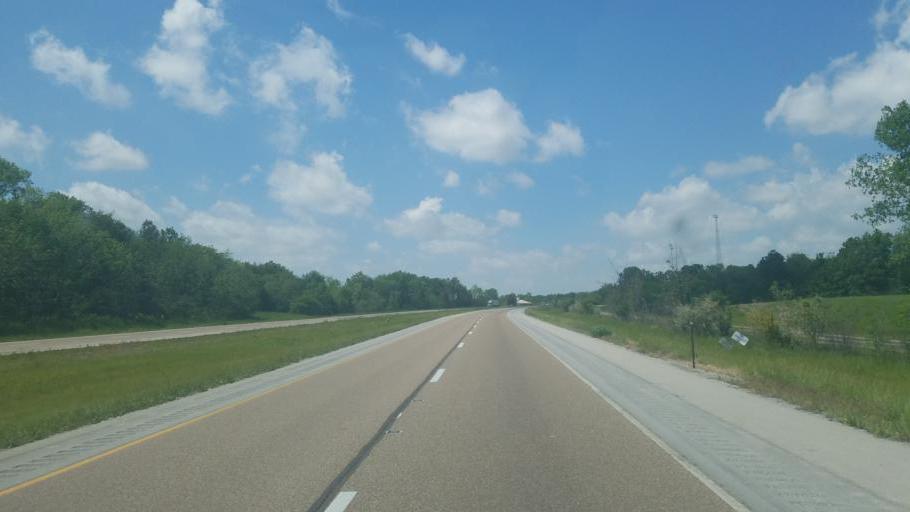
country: US
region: Illinois
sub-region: Cumberland County
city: Greenup
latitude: 39.2640
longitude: -88.1236
